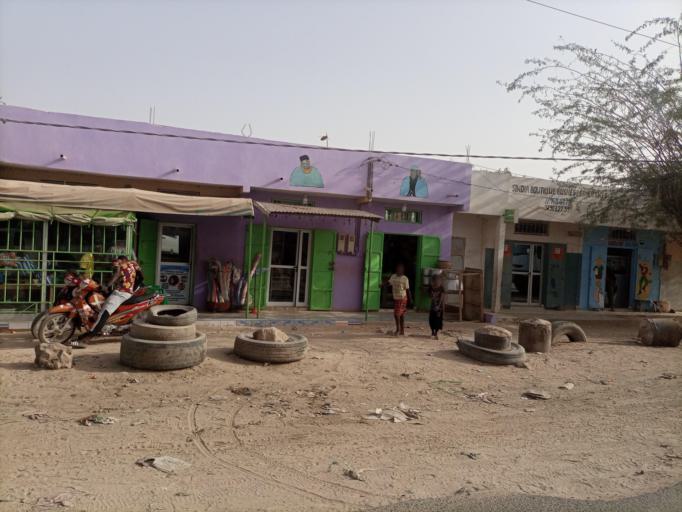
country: SN
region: Thies
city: Nguekhokh
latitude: 14.5833
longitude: -17.0335
